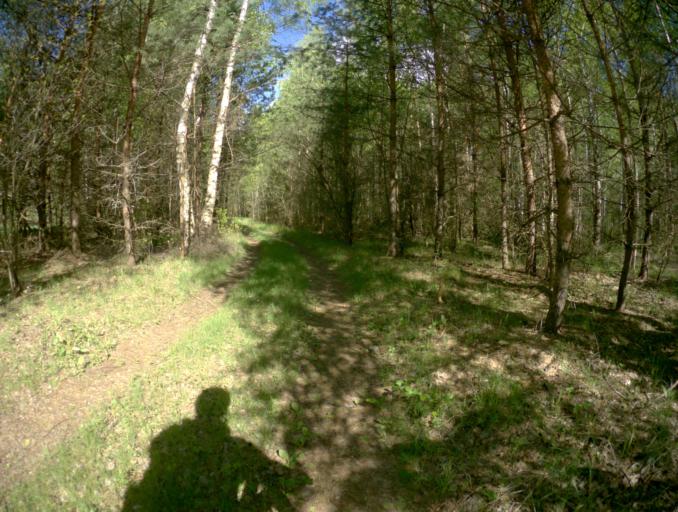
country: RU
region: Rjazan
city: Spas-Klepiki
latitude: 55.2479
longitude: 40.0986
